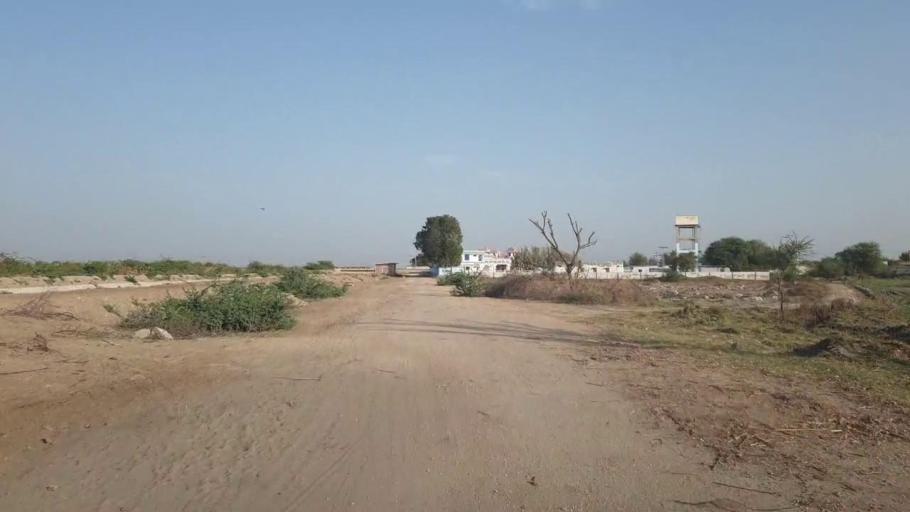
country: PK
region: Sindh
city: Dhoro Naro
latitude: 25.4845
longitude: 69.5844
